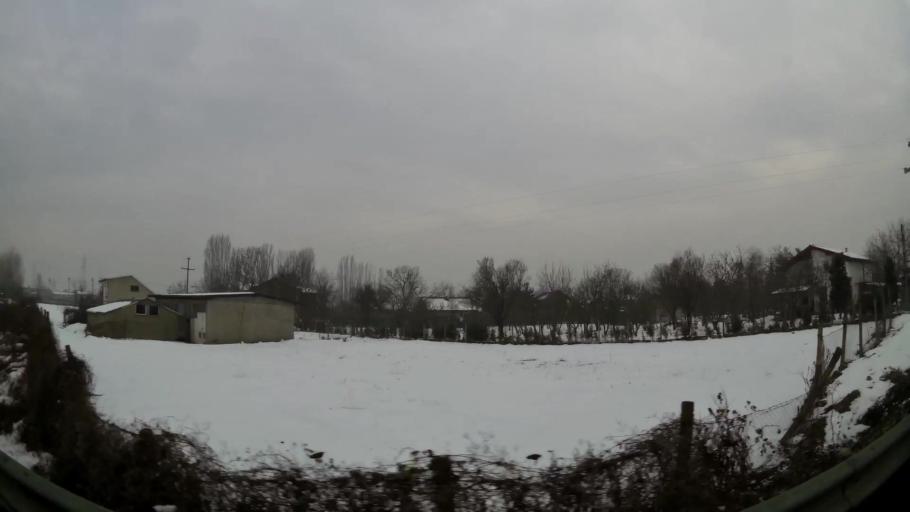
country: MK
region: Cucer-Sandevo
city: Chucher - Sandevo
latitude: 42.0473
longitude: 21.3662
